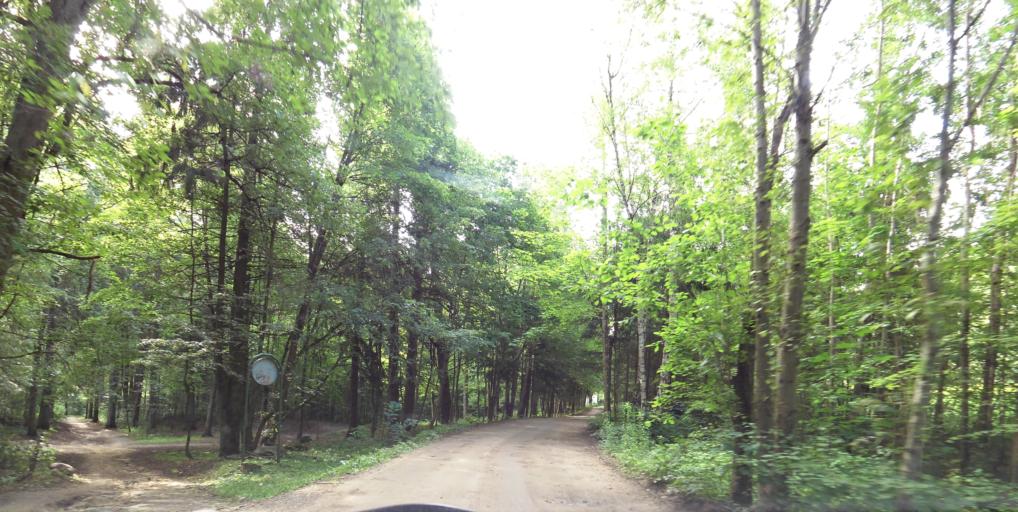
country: LT
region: Vilnius County
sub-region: Vilnius
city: Fabijoniskes
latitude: 54.7382
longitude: 25.2833
